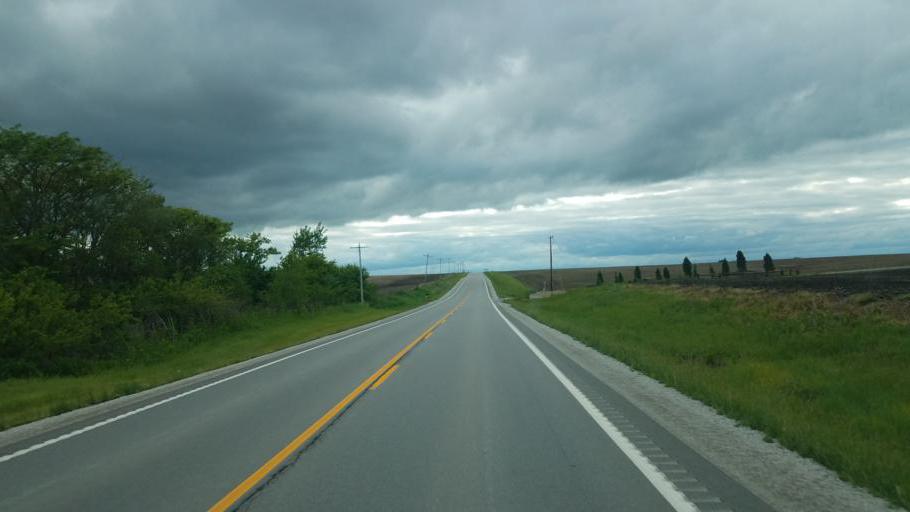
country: US
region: Missouri
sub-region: Harrison County
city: Bethany
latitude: 40.2644
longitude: -93.9413
